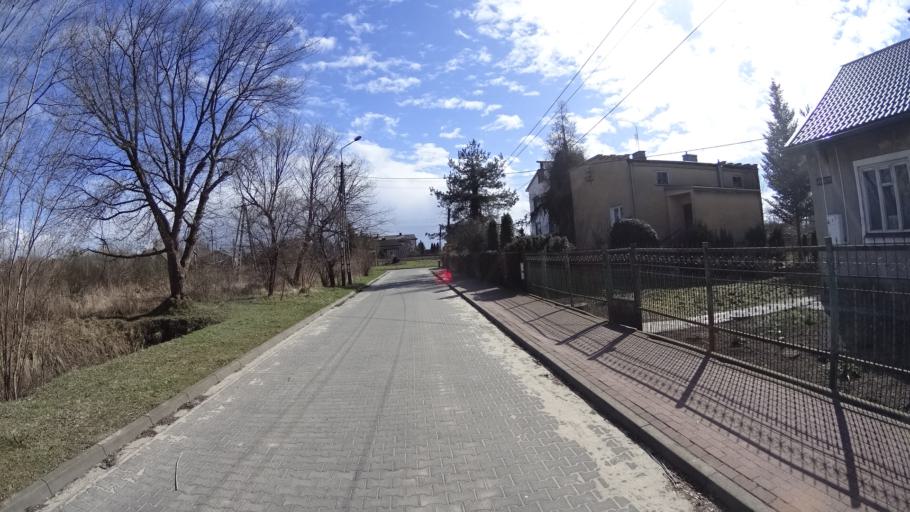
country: PL
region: Masovian Voivodeship
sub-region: Powiat warszawski zachodni
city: Jozefow
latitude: 52.2027
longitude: 20.7146
